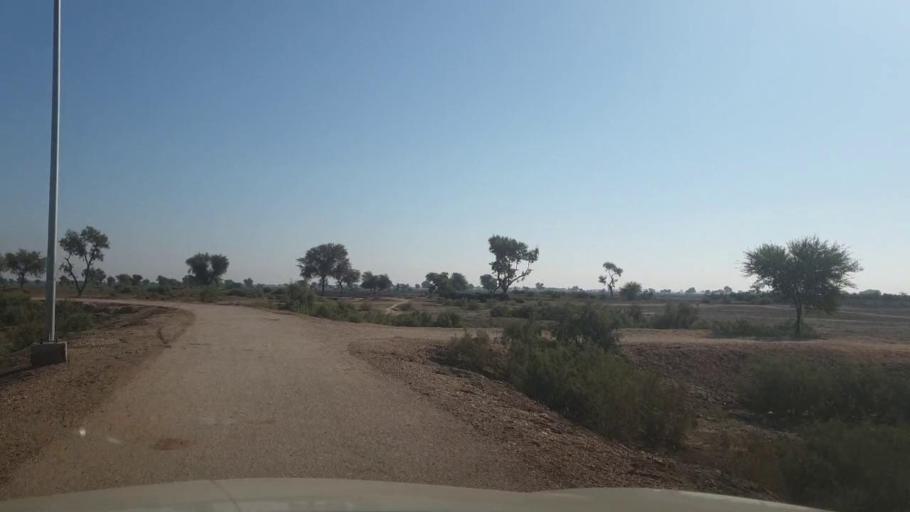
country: PK
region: Sindh
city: Bhan
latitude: 26.5350
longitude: 67.6574
